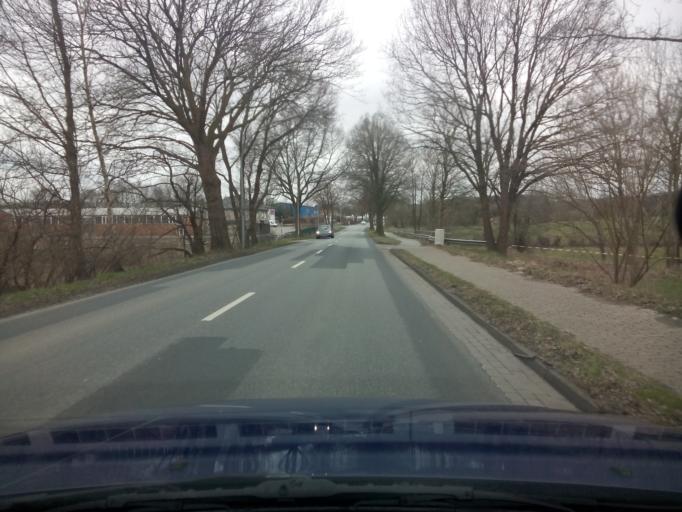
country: DE
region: Lower Saxony
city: Osterholz-Scharmbeck
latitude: 53.2386
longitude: 8.8127
